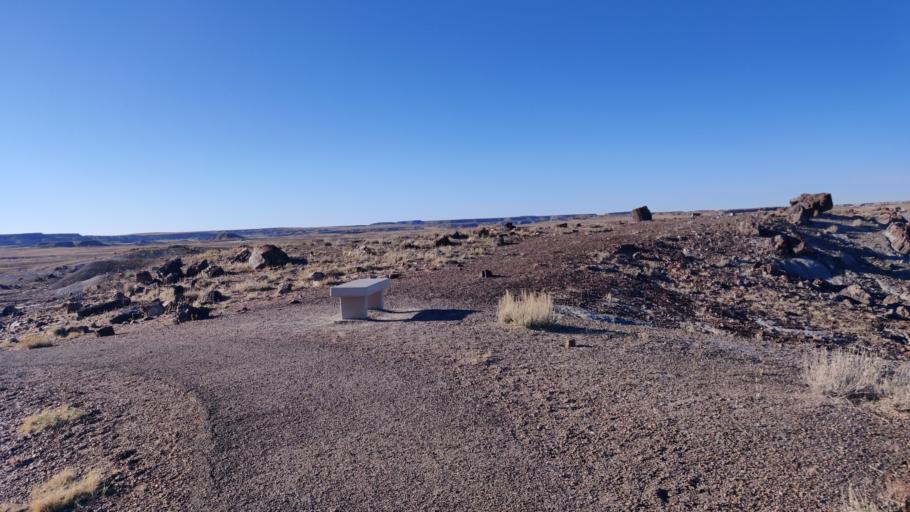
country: US
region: Arizona
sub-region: Navajo County
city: Holbrook
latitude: 34.8668
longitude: -109.7887
